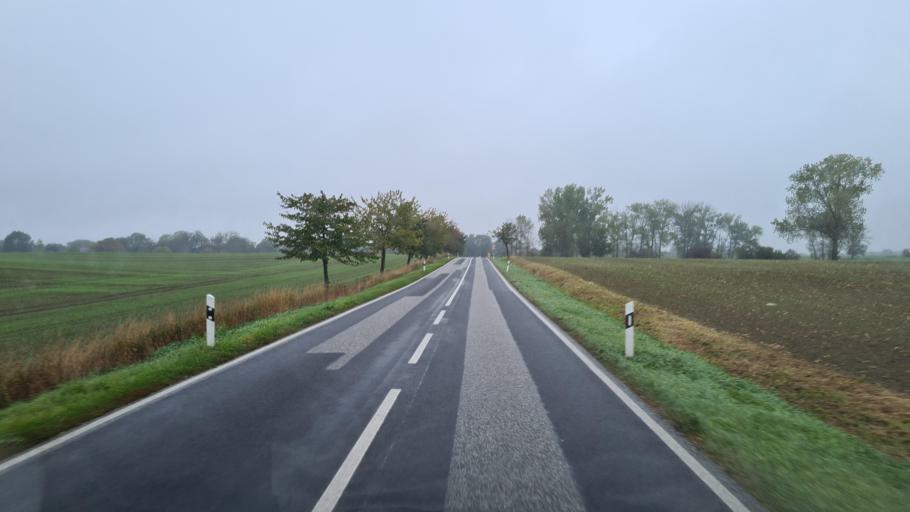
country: DE
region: Brandenburg
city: Furstenwalde
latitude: 52.4239
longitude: 14.0460
